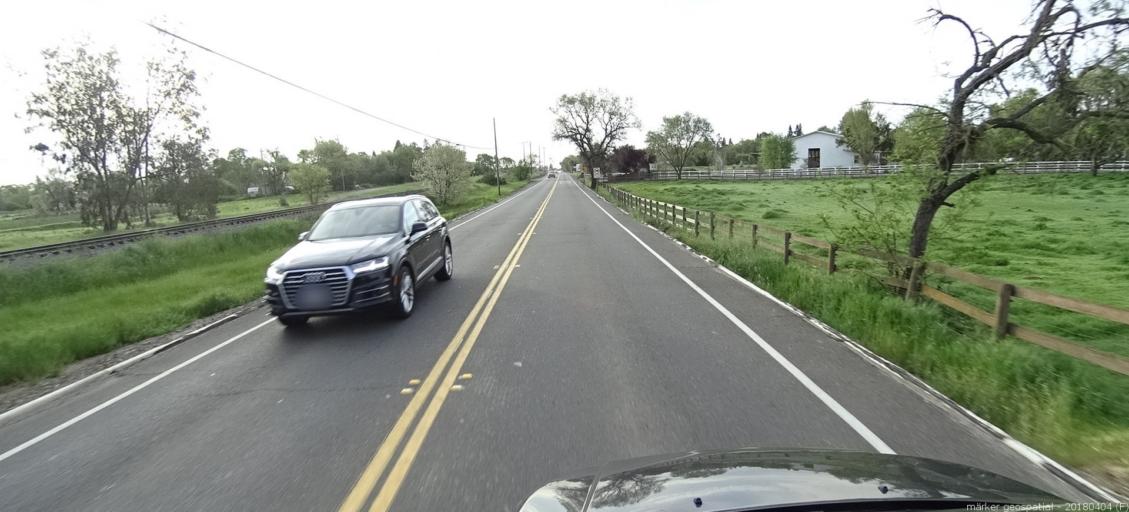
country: US
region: California
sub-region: Sacramento County
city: Wilton
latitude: 38.4135
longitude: -121.2748
